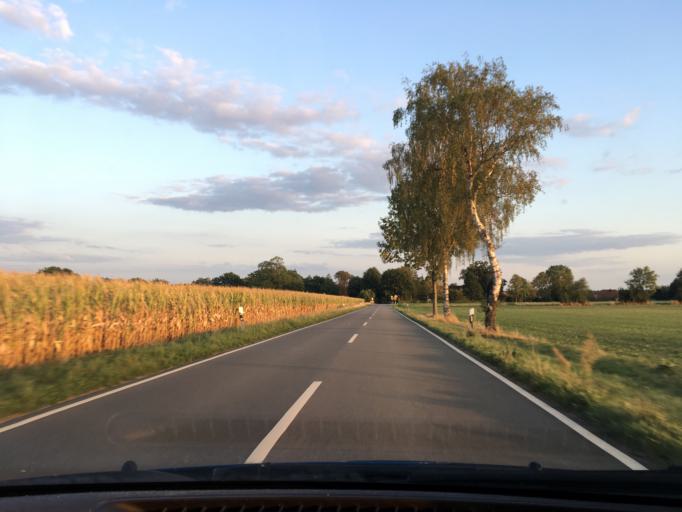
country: DE
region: Lower Saxony
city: Tosterglope
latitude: 53.2133
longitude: 10.8171
